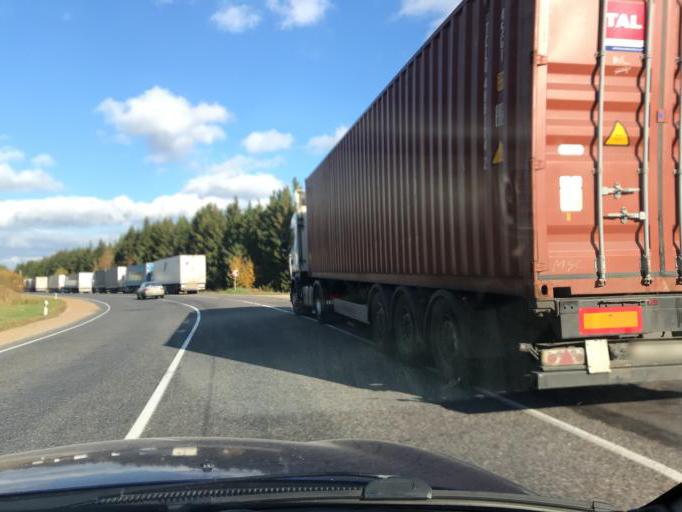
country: LT
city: Salcininkai
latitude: 54.2295
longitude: 25.3587
